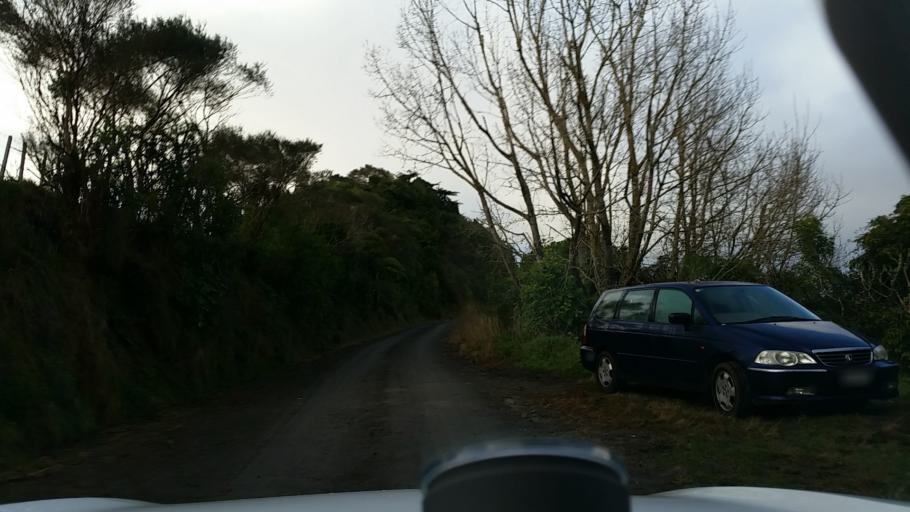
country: NZ
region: Taranaki
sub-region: South Taranaki District
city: Eltham
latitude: -39.4380
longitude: 174.4489
